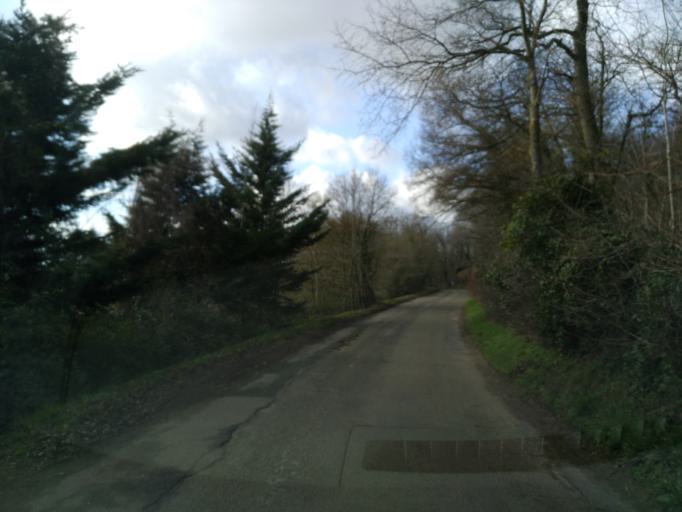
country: FR
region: Ile-de-France
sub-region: Departement des Yvelines
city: Saint-Nom-la-Breteche
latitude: 48.8722
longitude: 2.0065
